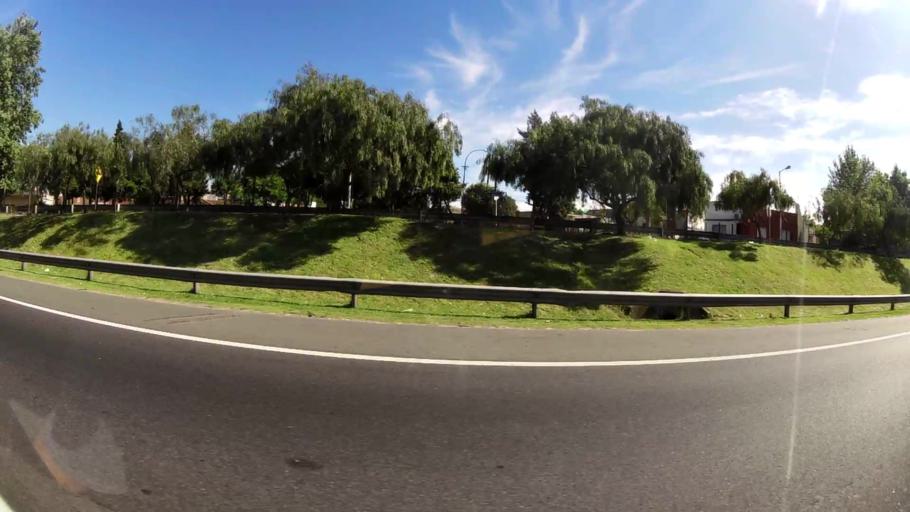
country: AR
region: Buenos Aires
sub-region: Partido de Moron
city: Moron
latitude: -34.6320
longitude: -58.5905
